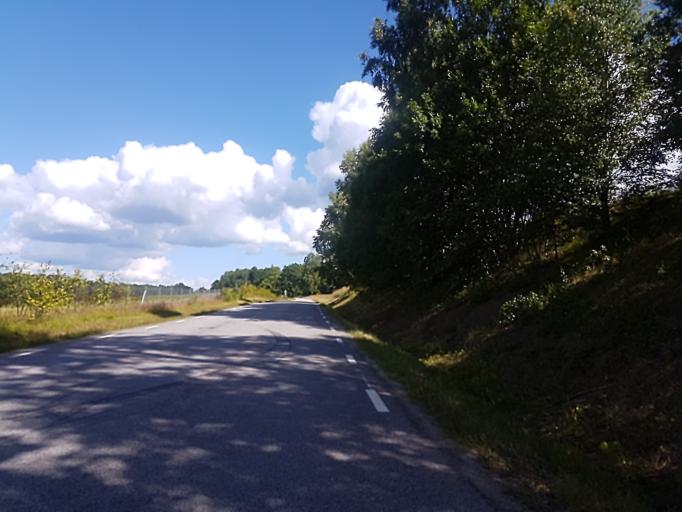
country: SE
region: Soedermanland
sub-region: Gnesta Kommun
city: Gnesta
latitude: 59.0465
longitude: 17.3382
